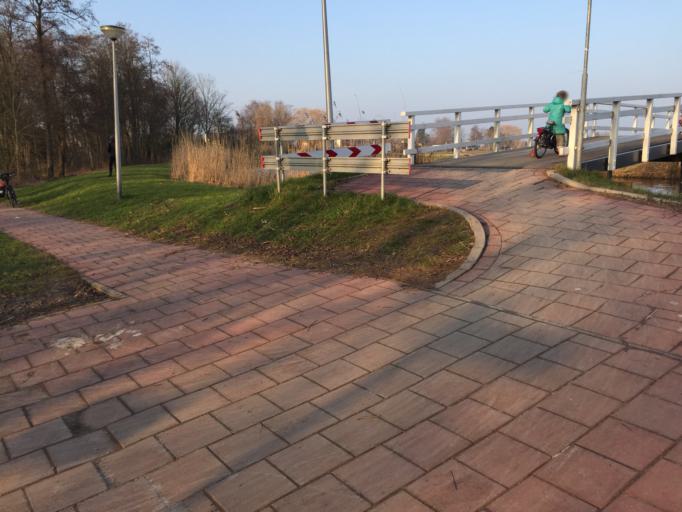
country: NL
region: South Holland
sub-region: Gemeente Vlist
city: Haastrecht
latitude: 51.9948
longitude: 4.7818
